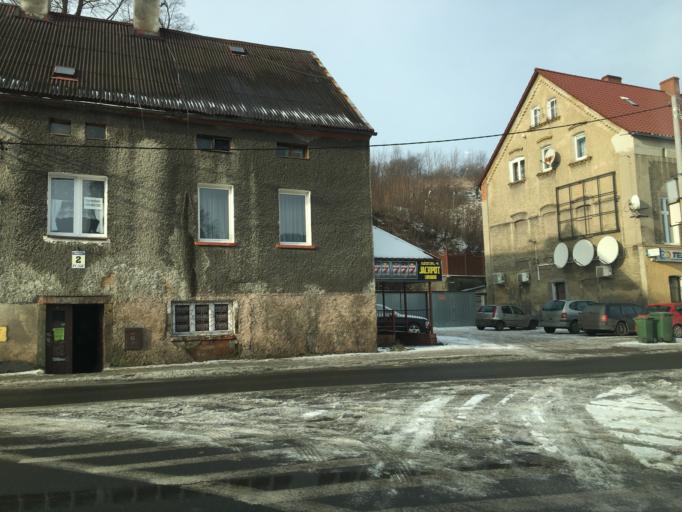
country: PL
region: Lower Silesian Voivodeship
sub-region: Powiat walbrzyski
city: Gluszyca
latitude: 50.6872
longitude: 16.3711
